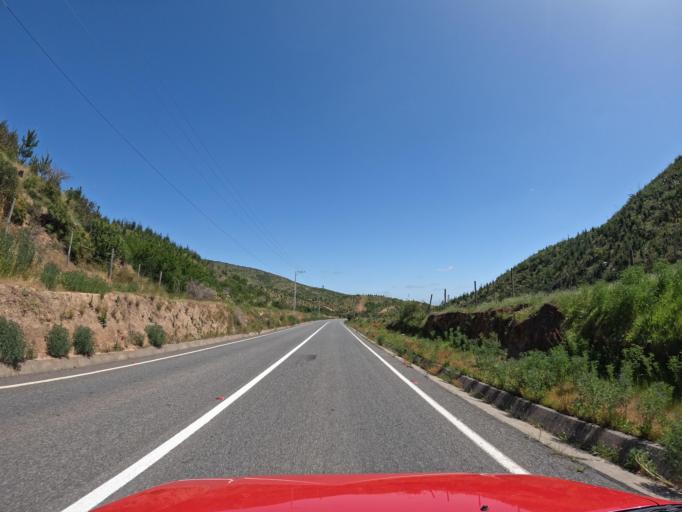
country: CL
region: O'Higgins
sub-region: Provincia de Colchagua
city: Santa Cruz
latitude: -34.6716
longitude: -71.8158
